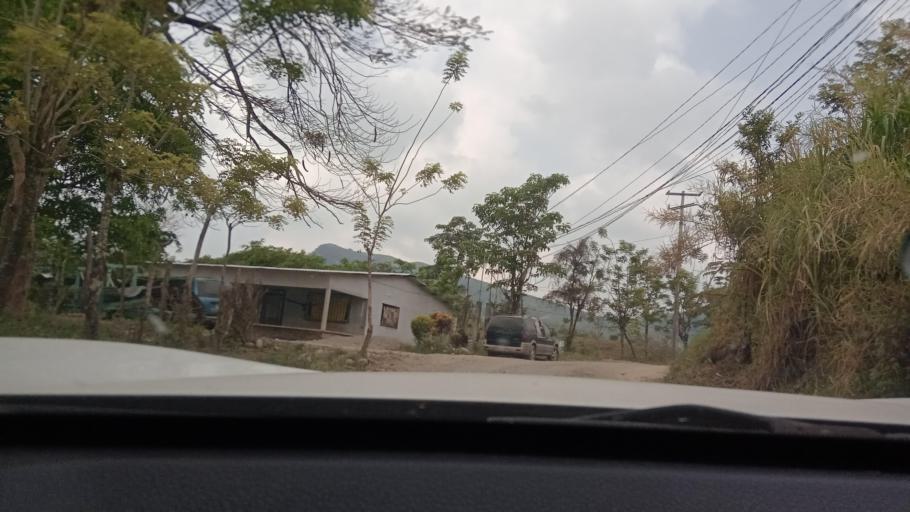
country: MX
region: Tabasco
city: Chontalpa
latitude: 17.5037
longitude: -93.6431
